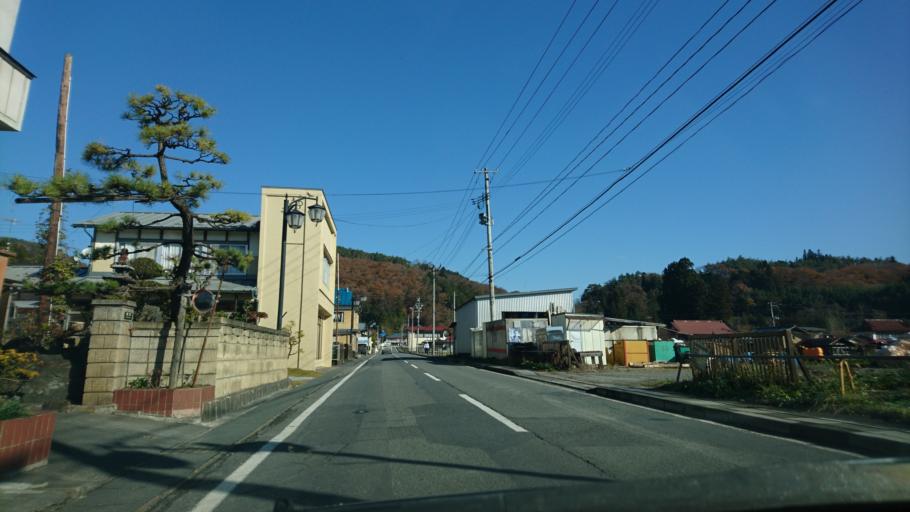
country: JP
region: Iwate
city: Ichinoseki
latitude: 38.9972
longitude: 141.2557
